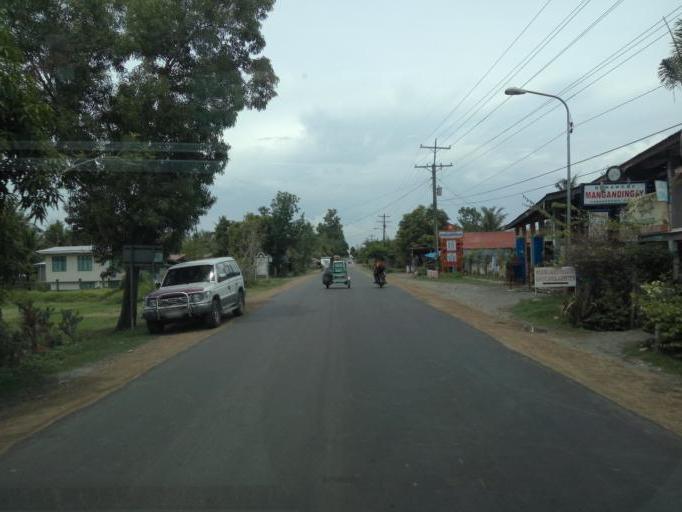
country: PH
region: Cagayan Valley
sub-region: Province of Quirino
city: Saguday
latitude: 16.5144
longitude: 121.5443
